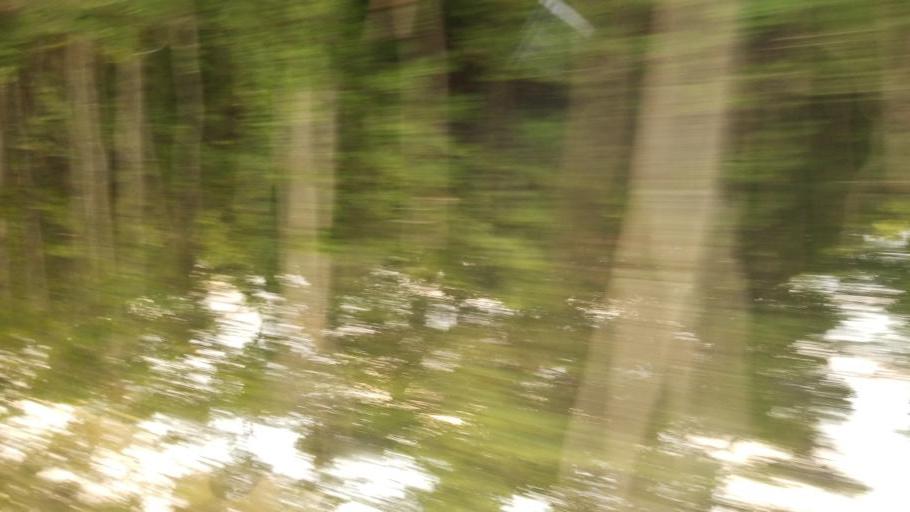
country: US
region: Virginia
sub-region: Culpeper County
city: Culpeper
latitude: 38.4852
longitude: -77.9503
